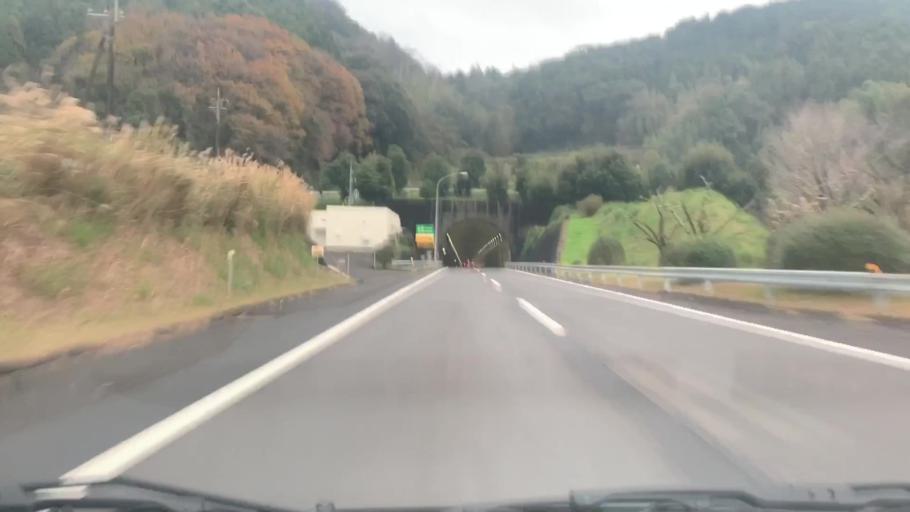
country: JP
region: Nagasaki
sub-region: Isahaya-shi
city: Isahaya
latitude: 32.8743
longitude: 129.9979
